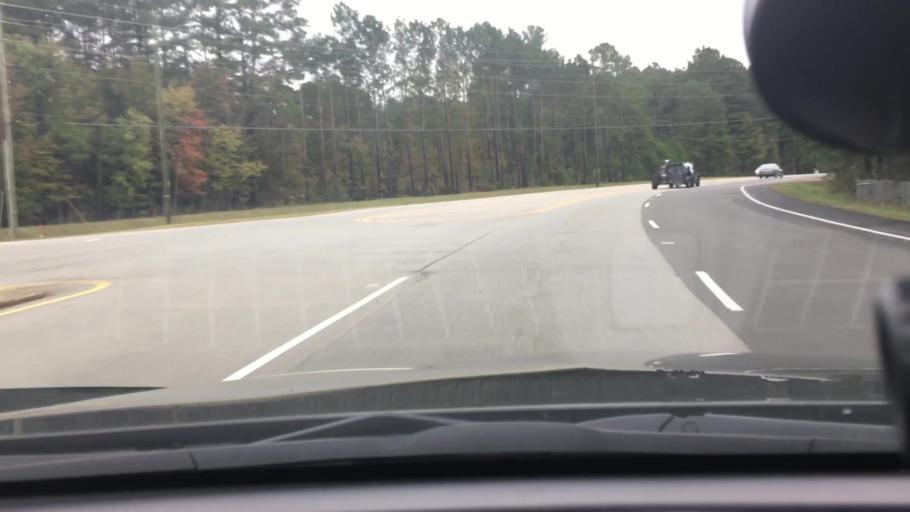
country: US
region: North Carolina
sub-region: Wake County
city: Apex
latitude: 35.6938
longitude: -78.8343
